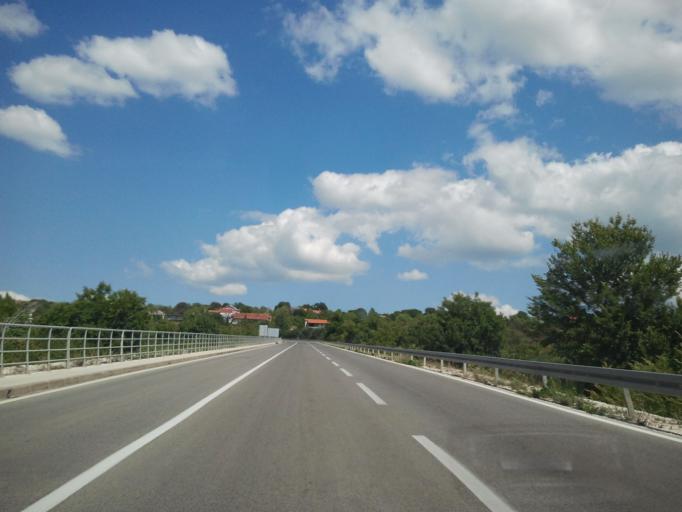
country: HR
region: Zadarska
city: Benkovac
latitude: 44.0345
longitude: 15.6179
